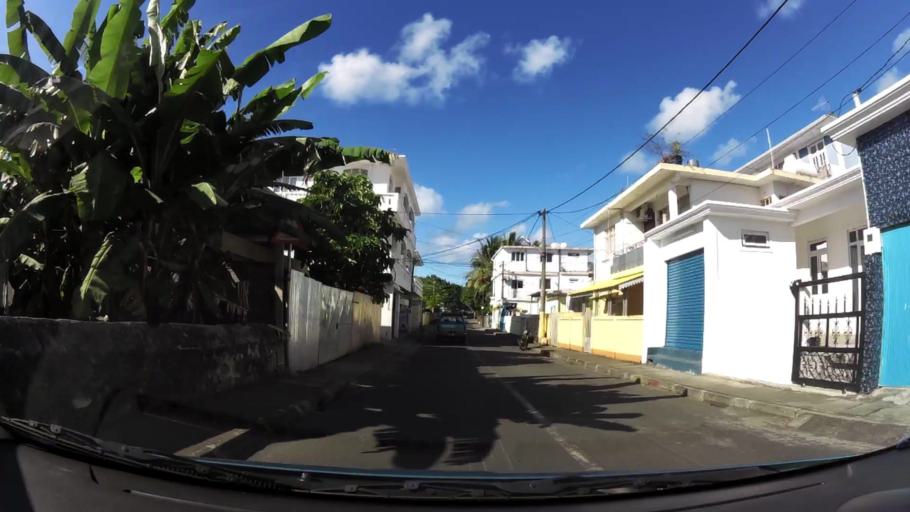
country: MU
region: Grand Port
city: Mahebourg
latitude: -20.4117
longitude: 57.7102
